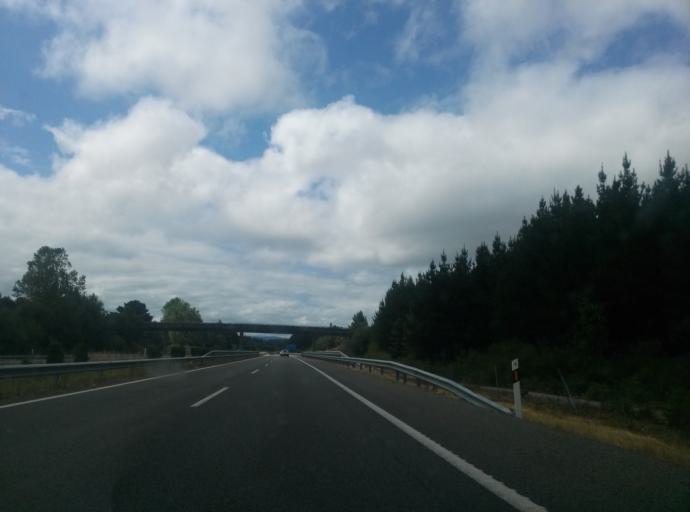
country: ES
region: Galicia
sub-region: Provincia de Lugo
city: Outeiro de Rei
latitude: 43.0936
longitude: -7.5898
